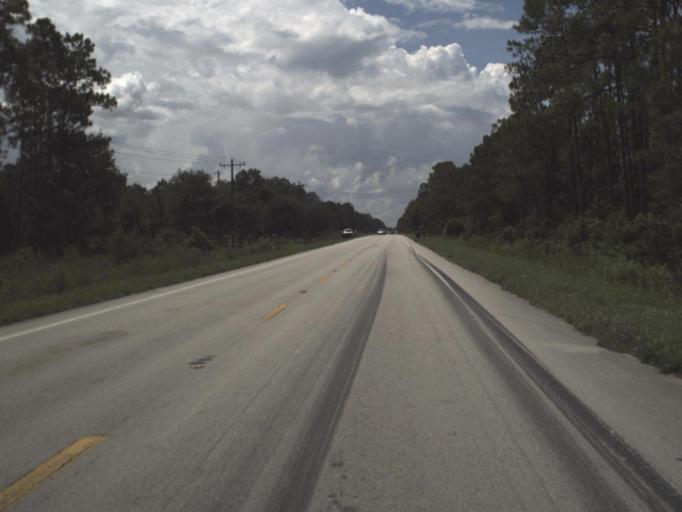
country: US
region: Florida
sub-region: Polk County
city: Babson Park
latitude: 27.8058
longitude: -81.2876
